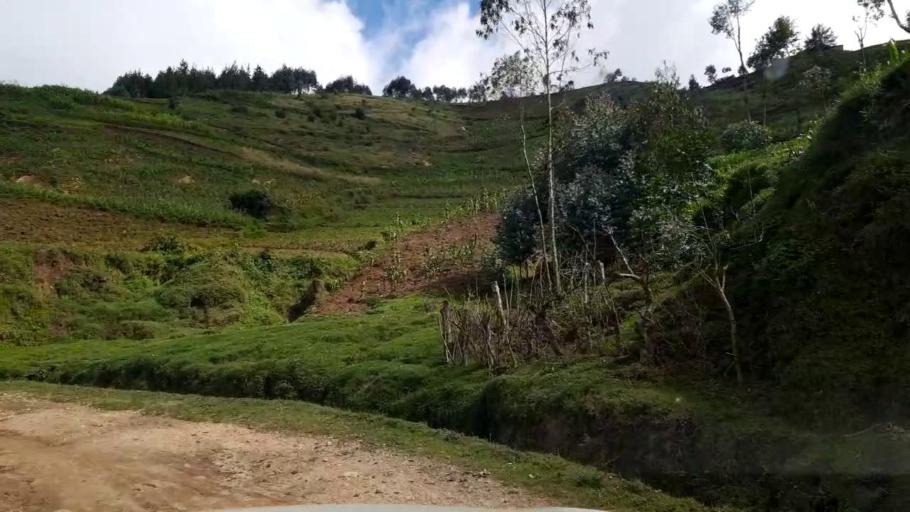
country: RW
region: Western Province
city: Kibuye
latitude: -1.8810
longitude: 29.4758
